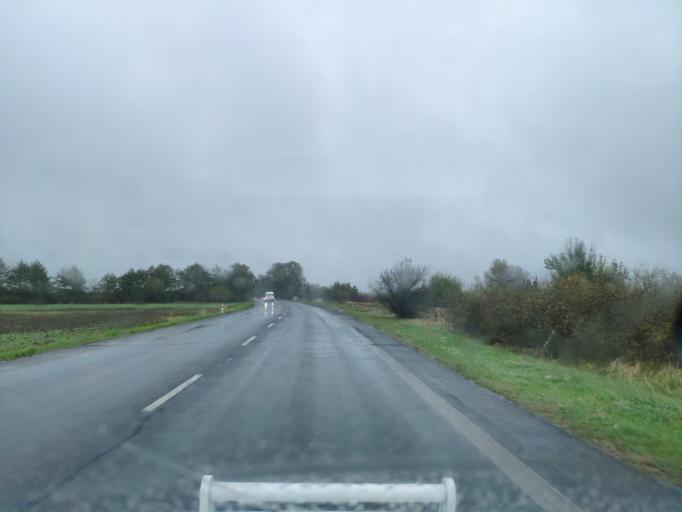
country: SK
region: Kosicky
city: Cierna nad Tisou
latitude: 48.4273
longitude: 21.9932
